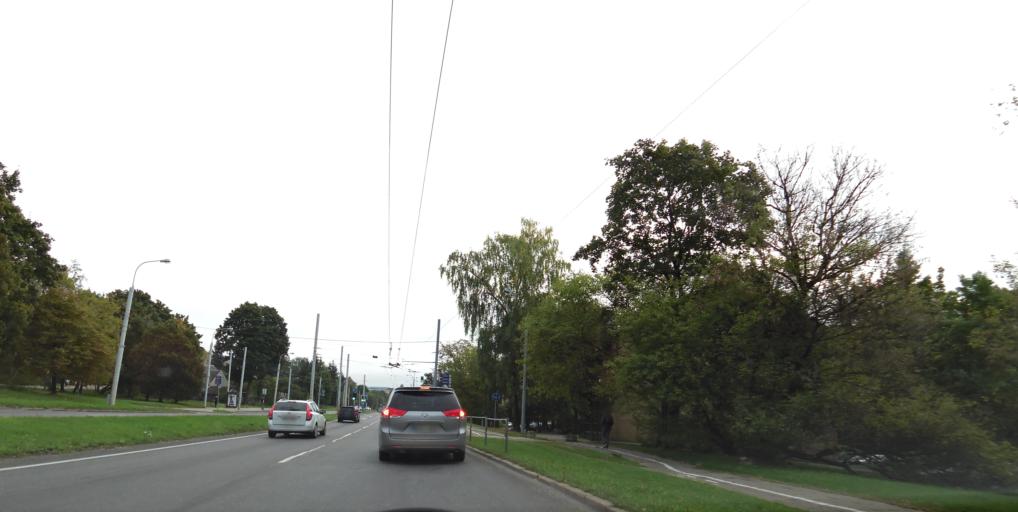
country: LT
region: Vilnius County
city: Seskine
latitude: 54.6992
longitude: 25.2418
